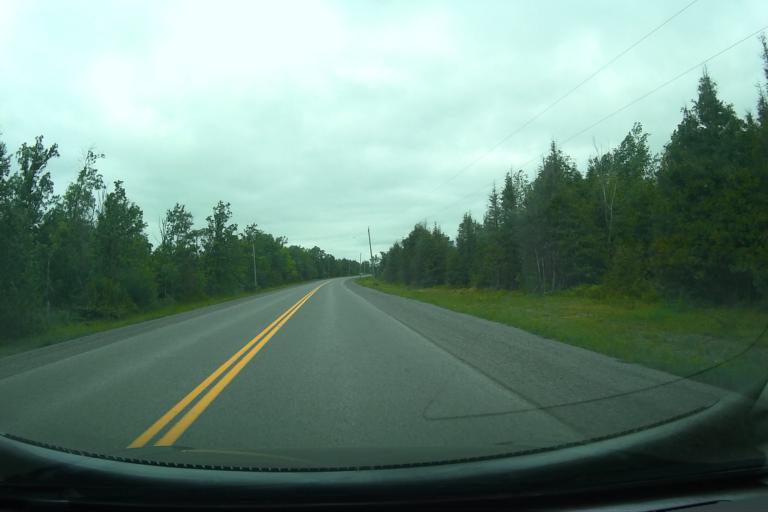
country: CA
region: Ontario
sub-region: Lanark County
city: Smiths Falls
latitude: 45.0284
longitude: -75.8589
